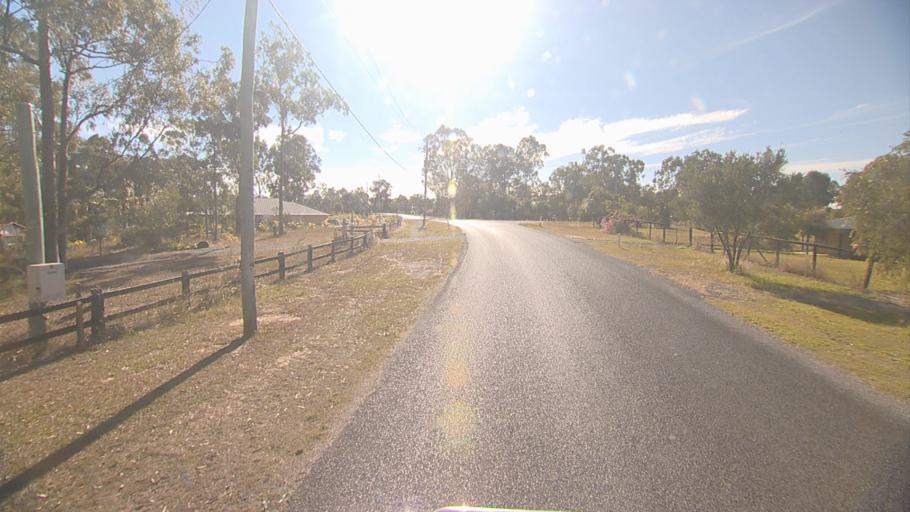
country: AU
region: Queensland
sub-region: Ipswich
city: Springfield Lakes
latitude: -27.6975
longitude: 152.9314
